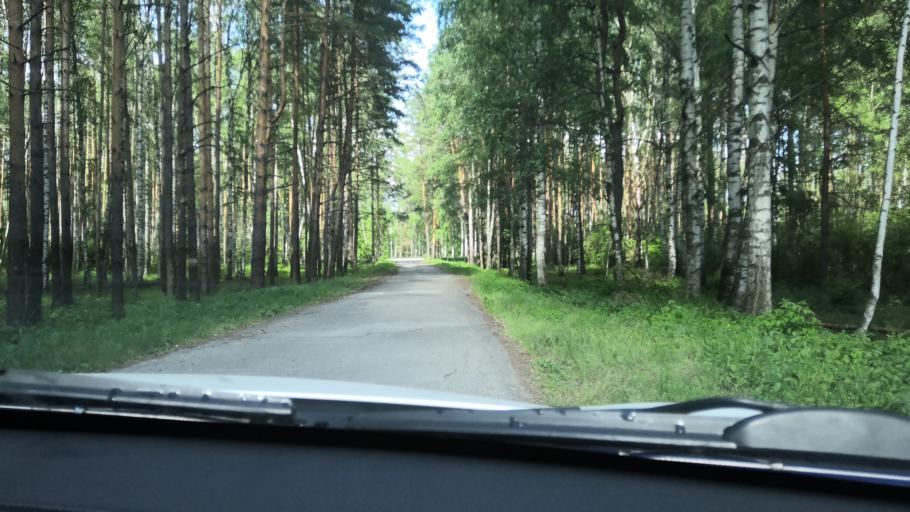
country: RU
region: Rjazan
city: Murmino
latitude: 54.5390
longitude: 40.1725
